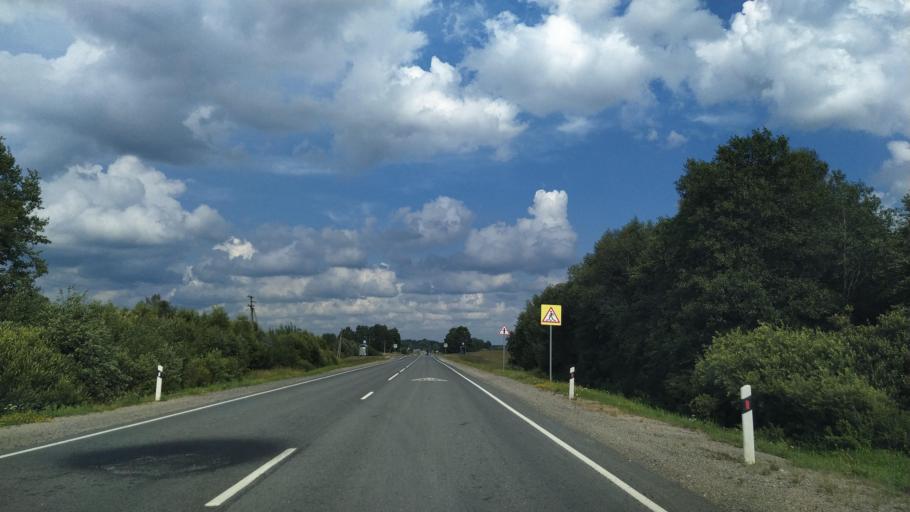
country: RU
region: Novgorod
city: Sol'tsy
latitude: 58.0979
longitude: 30.1830
